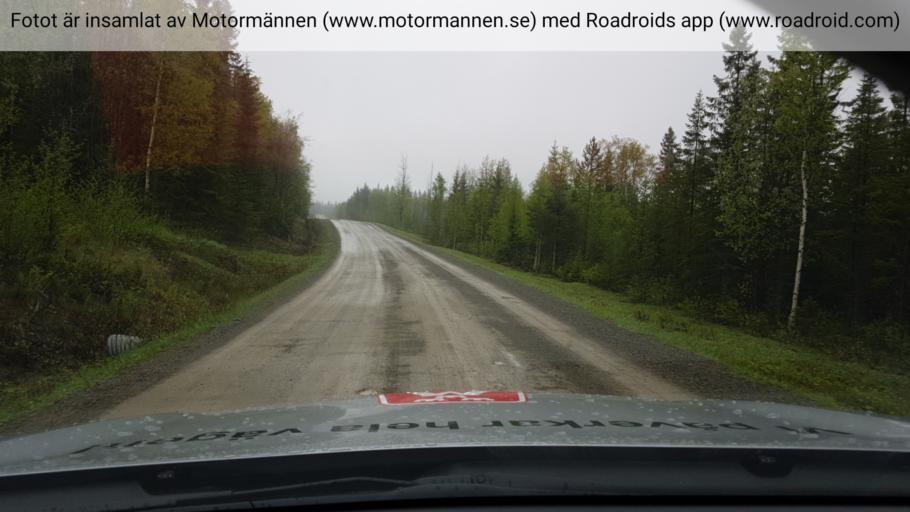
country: SE
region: Jaemtland
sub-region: Bergs Kommun
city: Hoverberg
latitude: 62.9978
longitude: 14.1512
